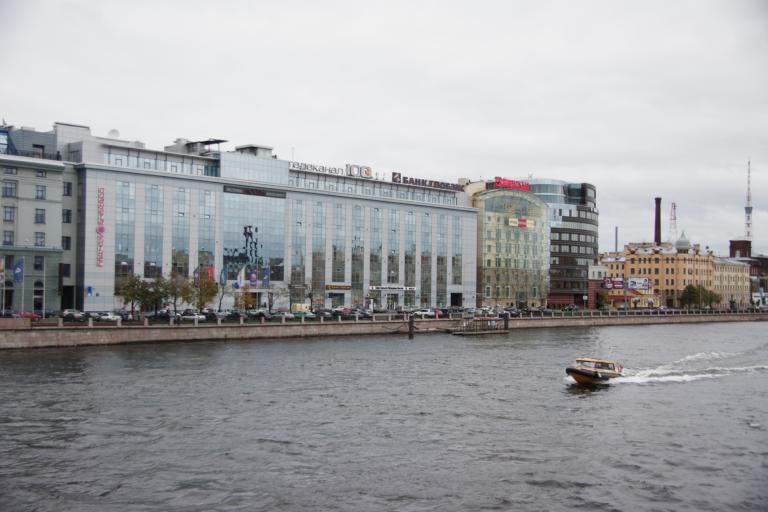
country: RU
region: St.-Petersburg
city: Petrogradka
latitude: 59.9581
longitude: 30.3375
